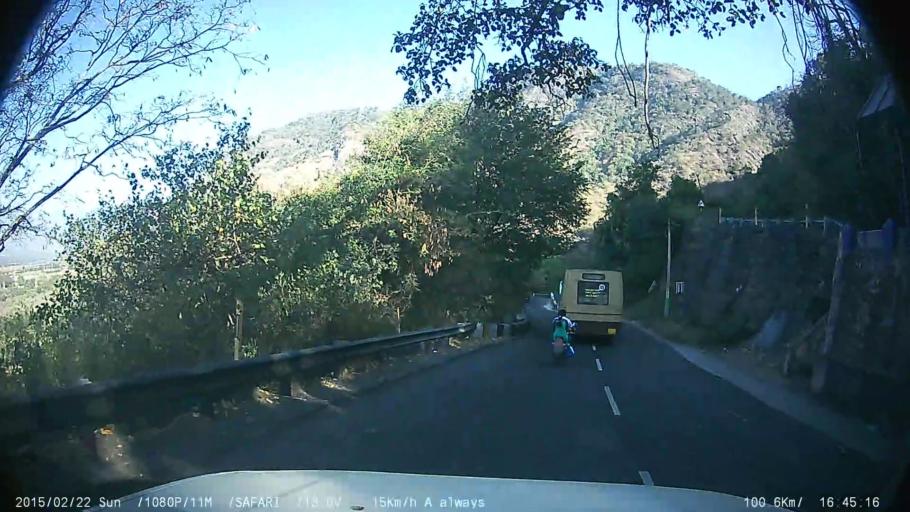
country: IN
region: Tamil Nadu
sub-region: Theni
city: Gudalur
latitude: 9.6230
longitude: 77.1884
